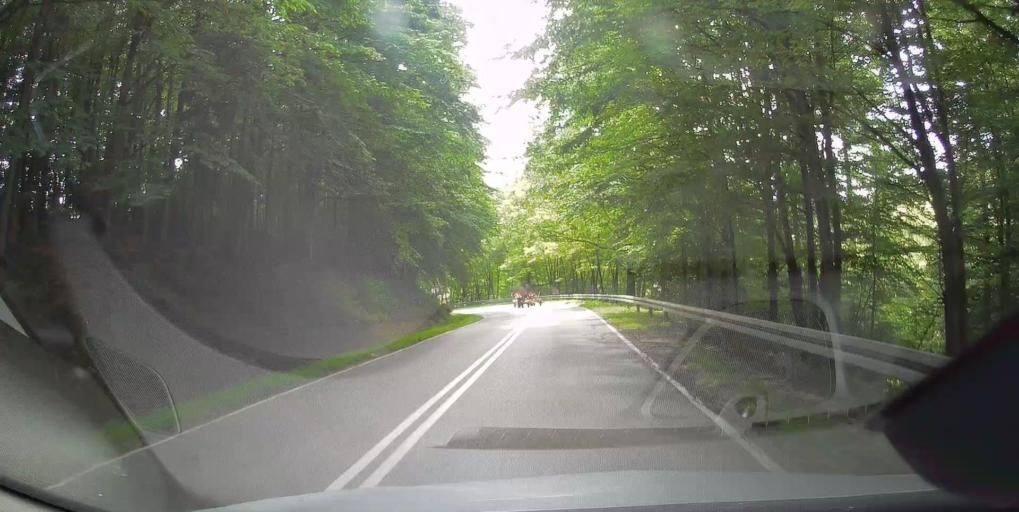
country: PL
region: Lesser Poland Voivodeship
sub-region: Powiat tarnowski
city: Zakliczyn
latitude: 49.7640
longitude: 20.7818
